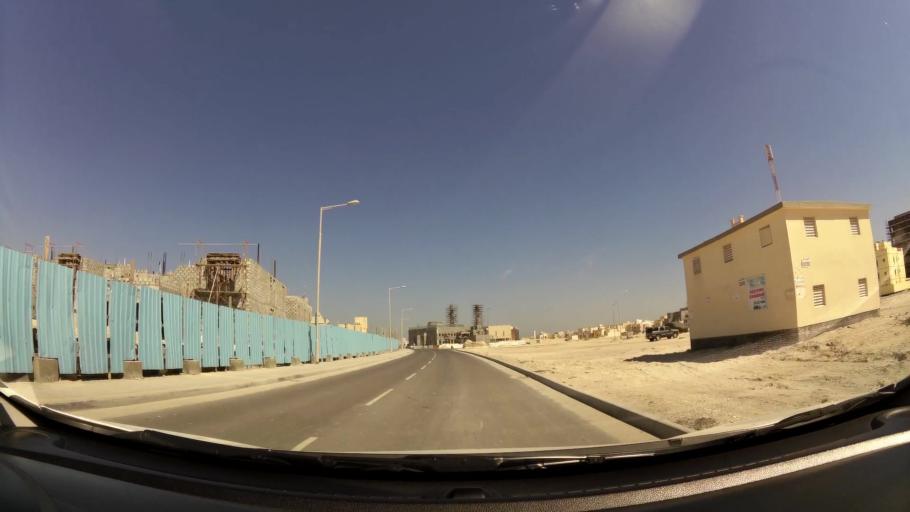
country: BH
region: Muharraq
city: Al Muharraq
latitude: 26.2735
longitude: 50.5985
